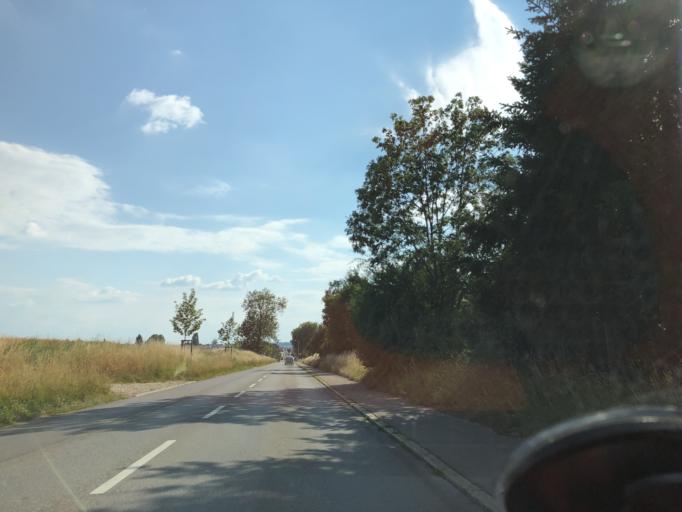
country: DE
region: Baden-Wuerttemberg
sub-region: Regierungsbezirk Stuttgart
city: Leinfelden-Echterdingen
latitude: 48.7348
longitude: 9.1614
